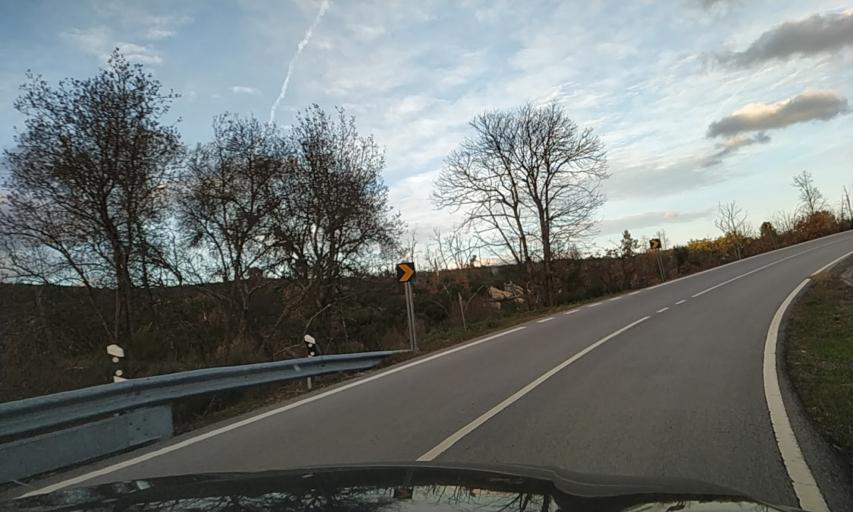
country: PT
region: Braganca
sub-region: Carrazeda de Ansiaes
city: Carrazeda de Anciaes
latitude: 41.2091
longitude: -7.3348
